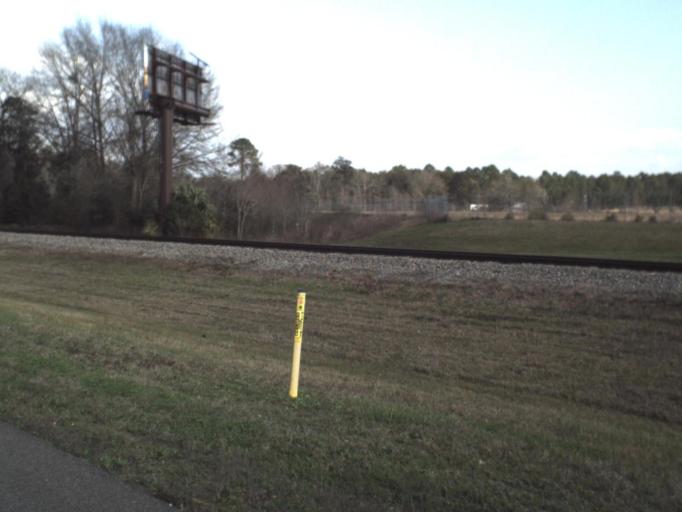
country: US
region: Florida
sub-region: Bay County
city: Hiland Park
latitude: 30.2277
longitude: -85.5867
